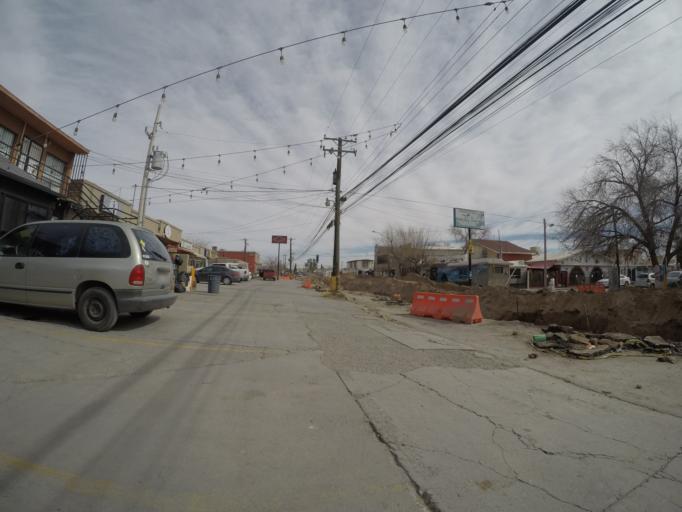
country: MX
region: Chihuahua
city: Ciudad Juarez
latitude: 31.7210
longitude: -106.4284
